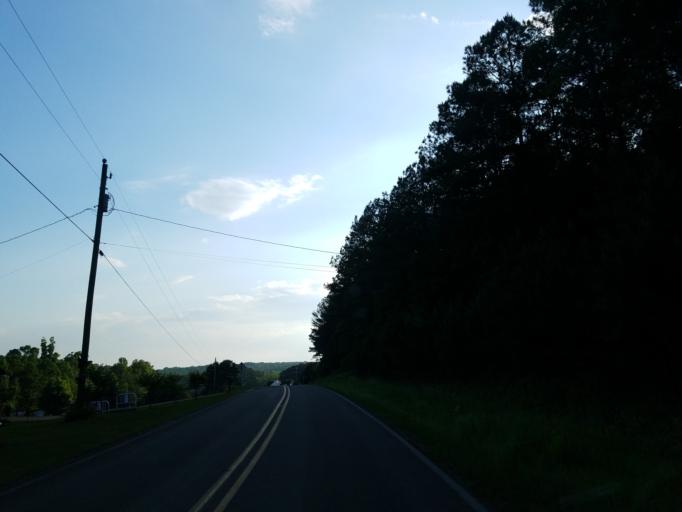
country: US
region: Georgia
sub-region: Cherokee County
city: Ball Ground
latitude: 34.3002
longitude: -84.3703
